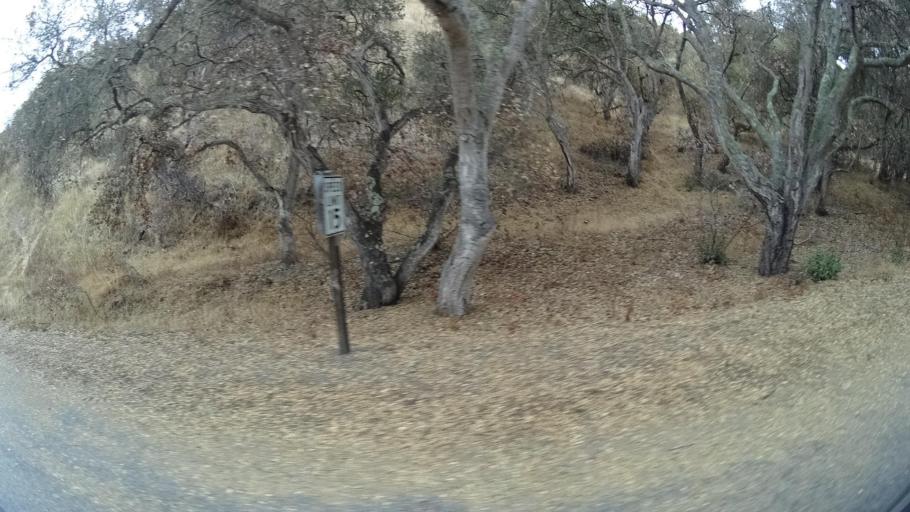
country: US
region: California
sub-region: Monterey County
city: Salinas
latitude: 36.5924
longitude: -121.6932
